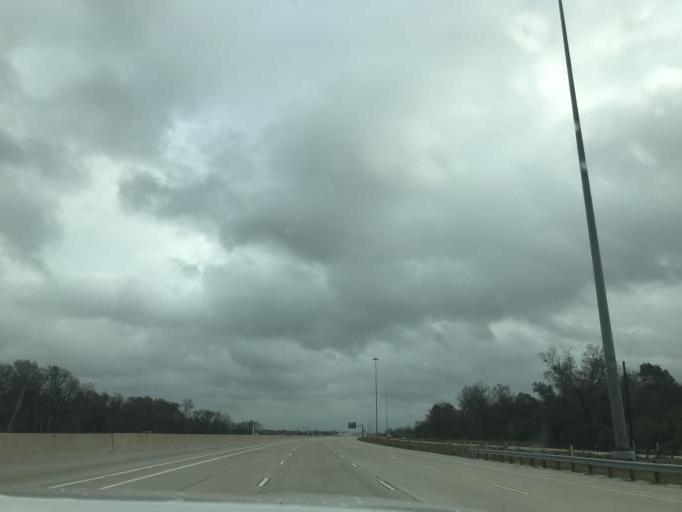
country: US
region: Texas
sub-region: Fort Bend County
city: Richmond
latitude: 29.5526
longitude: -95.7316
